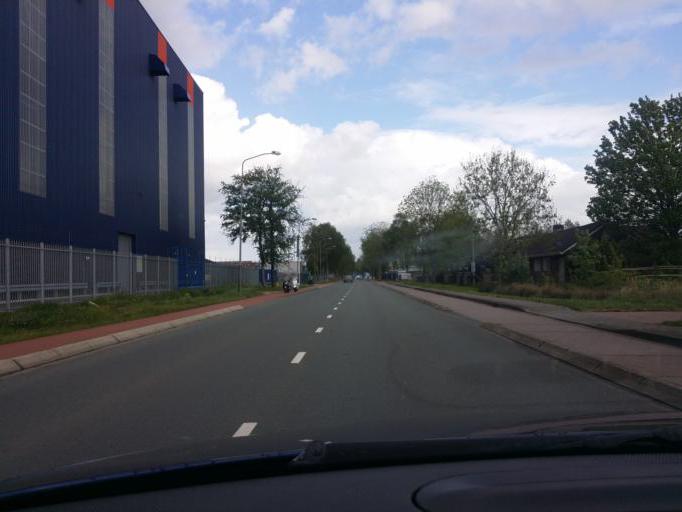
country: NL
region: Groningen
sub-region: Gemeente Hoogezand-Sappemeer
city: Hoogezand
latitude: 53.1673
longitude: 6.7299
